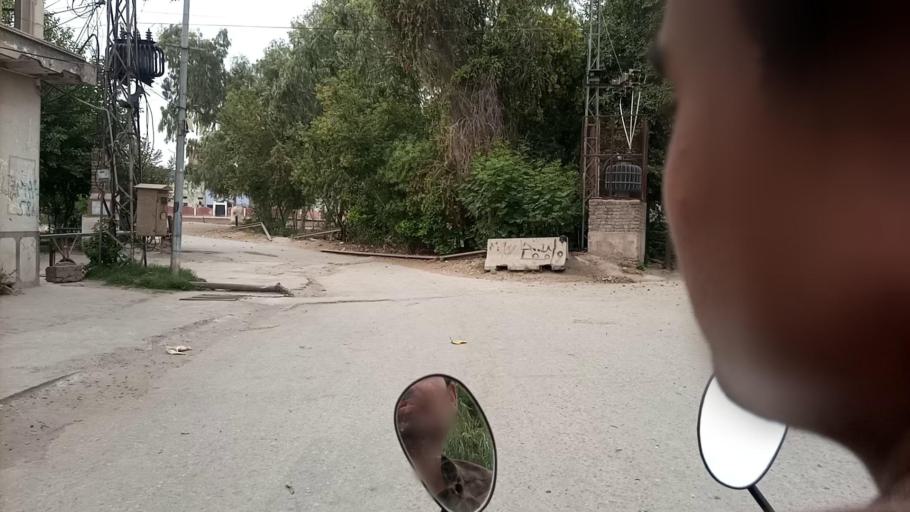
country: PK
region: Khyber Pakhtunkhwa
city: Peshawar
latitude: 34.0172
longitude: 71.5918
